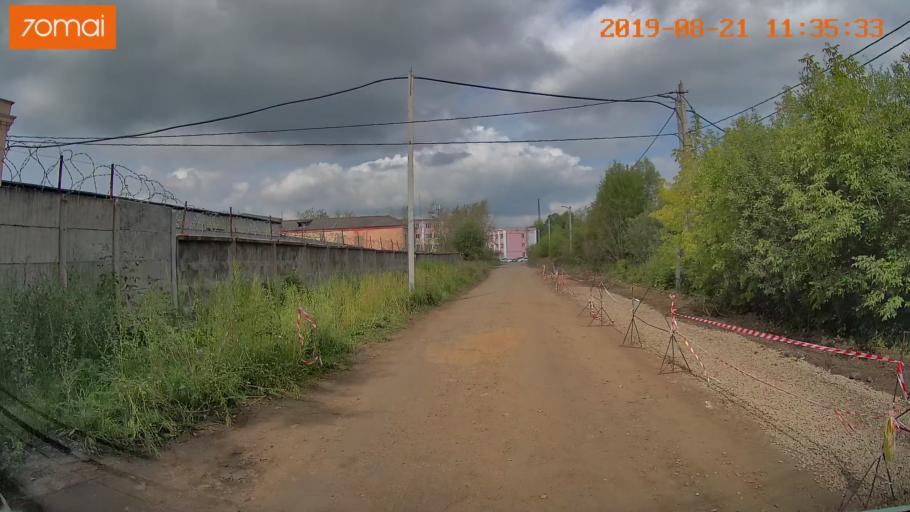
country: RU
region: Ivanovo
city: Novo-Talitsy
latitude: 56.9900
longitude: 40.9102
